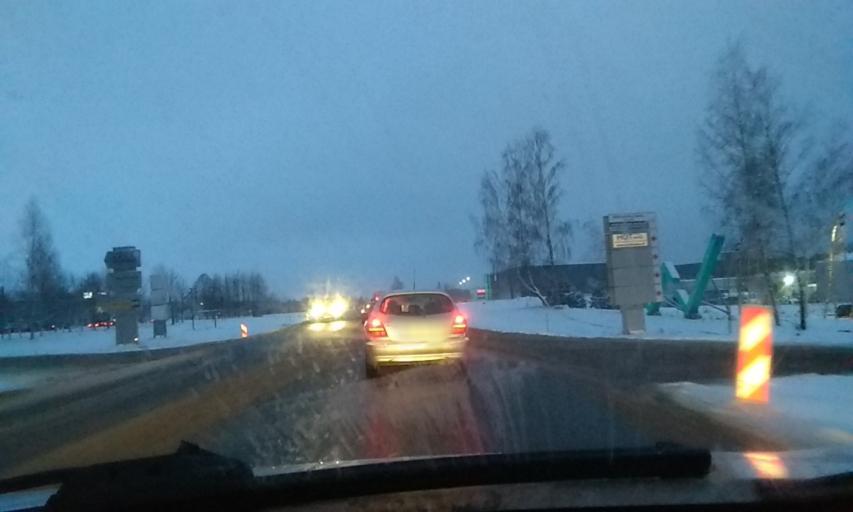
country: LT
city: Ramuciai
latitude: 54.9074
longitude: 24.0306
